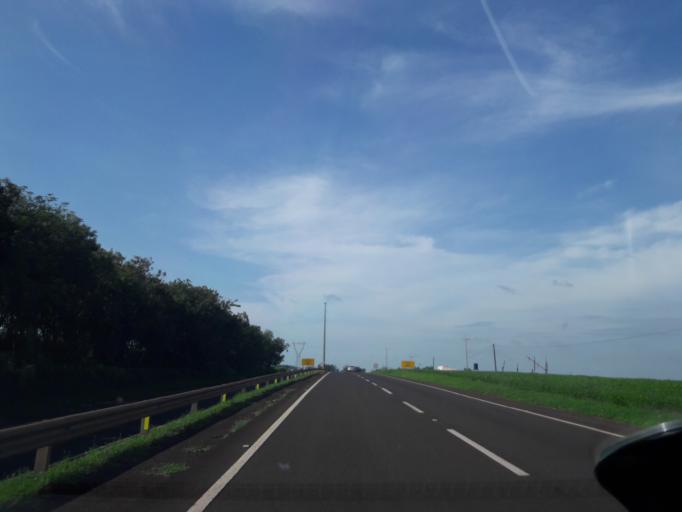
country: BR
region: Parana
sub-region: Paicandu
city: Paicandu
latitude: -23.5989
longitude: -52.0796
